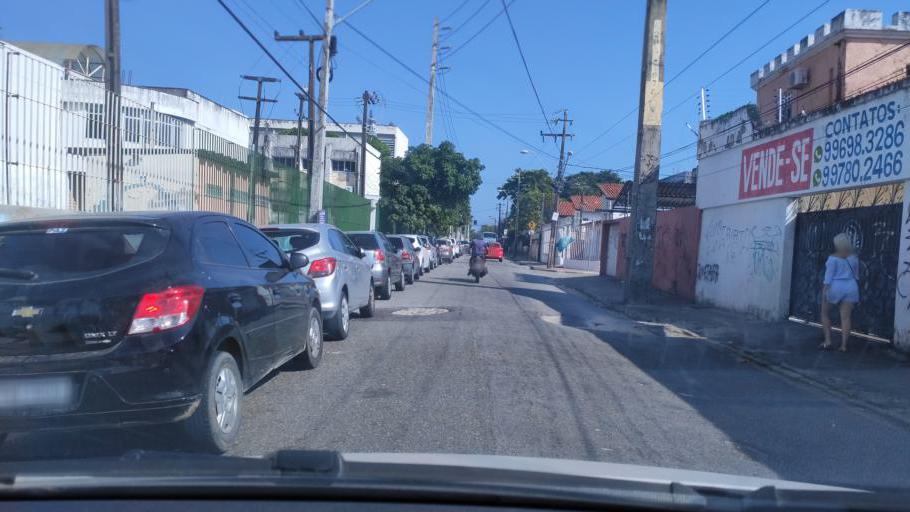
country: BR
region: Ceara
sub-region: Fortaleza
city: Fortaleza
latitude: -3.7408
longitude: -38.5371
